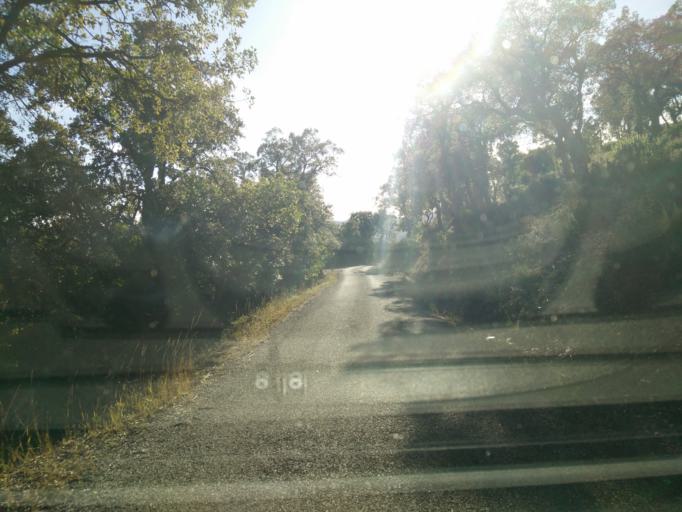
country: FR
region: Provence-Alpes-Cote d'Azur
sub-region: Departement du Var
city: Collobrieres
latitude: 43.2621
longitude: 6.2897
